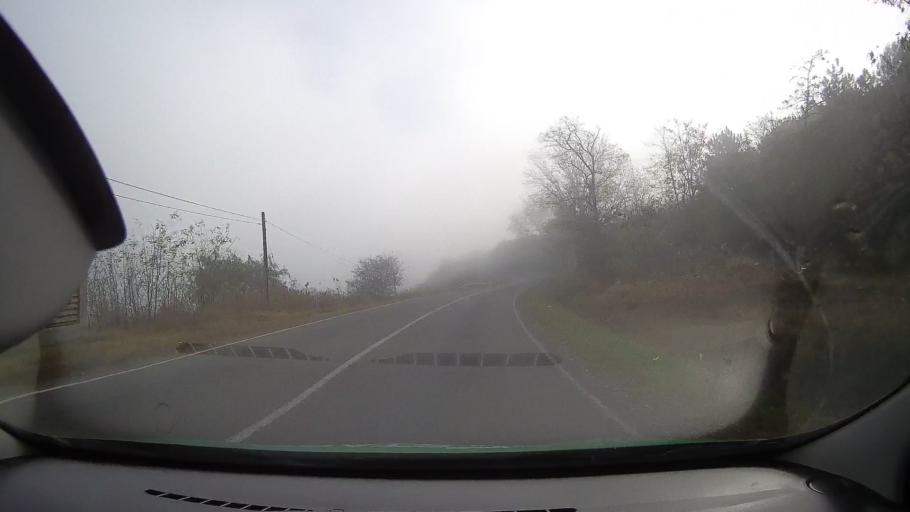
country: RO
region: Tulcea
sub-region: Municipiul Tulcea
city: Tulcea
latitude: 45.1674
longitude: 28.8369
